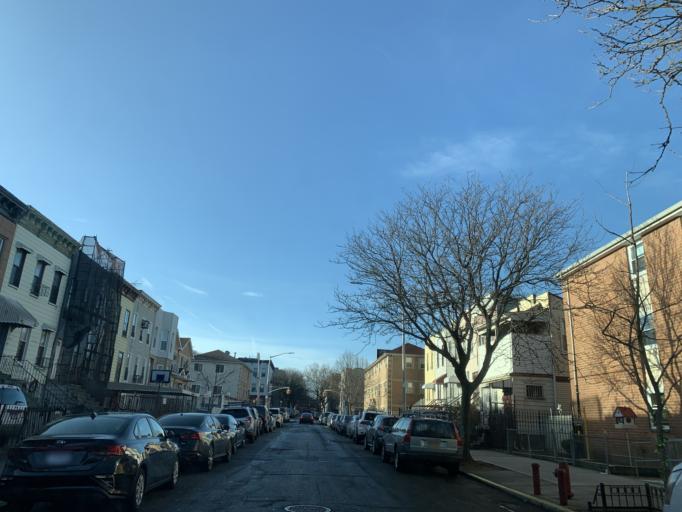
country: US
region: New York
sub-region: Kings County
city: East New York
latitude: 40.6871
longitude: -73.9116
